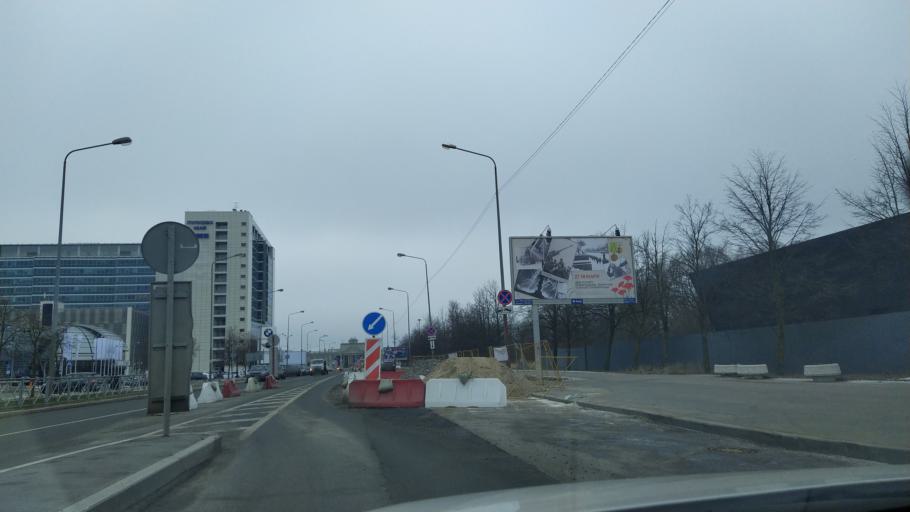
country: RU
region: St.-Petersburg
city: Kupchino
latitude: 59.8083
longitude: 30.3140
